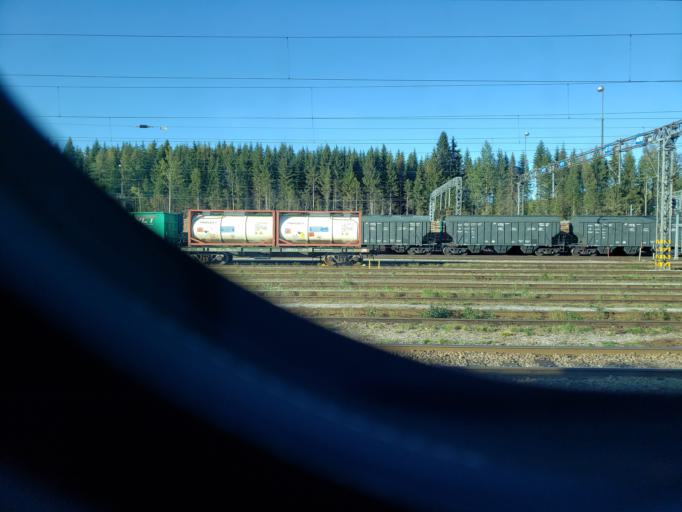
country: FI
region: South Karelia
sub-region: Lappeenranta
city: Lappeenranta
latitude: 60.8614
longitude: 28.3141
